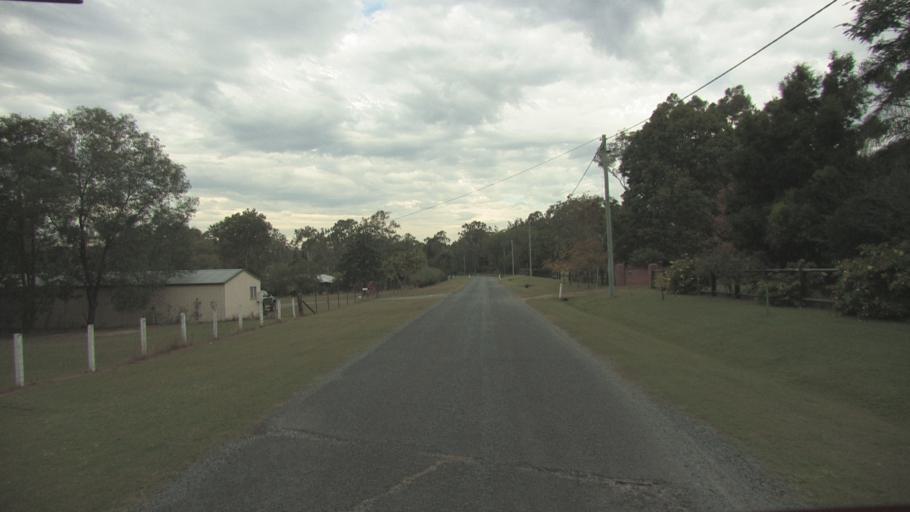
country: AU
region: Queensland
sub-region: Logan
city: Chambers Flat
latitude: -27.7917
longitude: 153.1113
